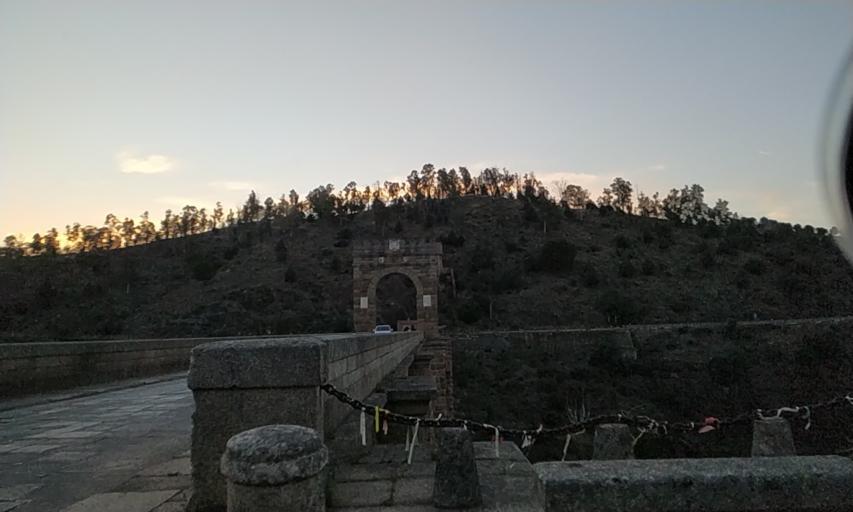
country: ES
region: Extremadura
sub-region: Provincia de Caceres
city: Alcantara
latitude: 39.7218
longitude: -6.8916
